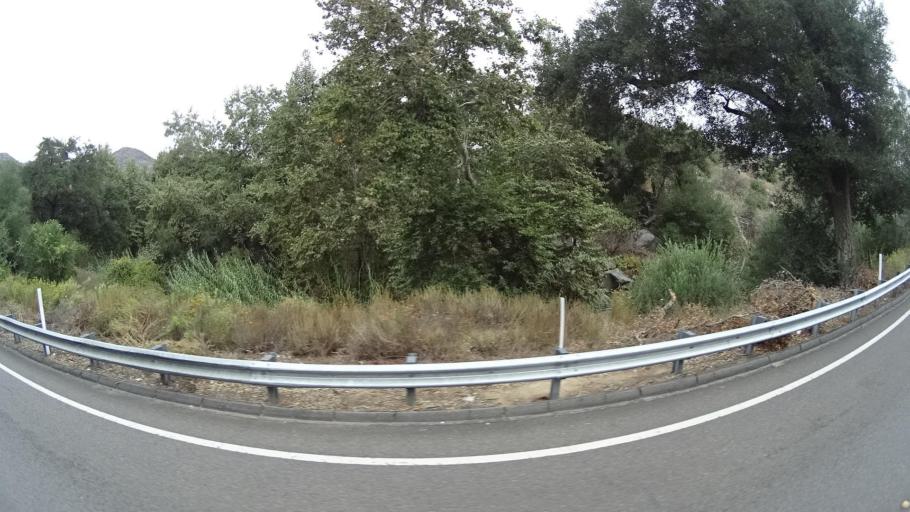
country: US
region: California
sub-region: San Diego County
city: Ramona
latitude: 33.0724
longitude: -116.9020
